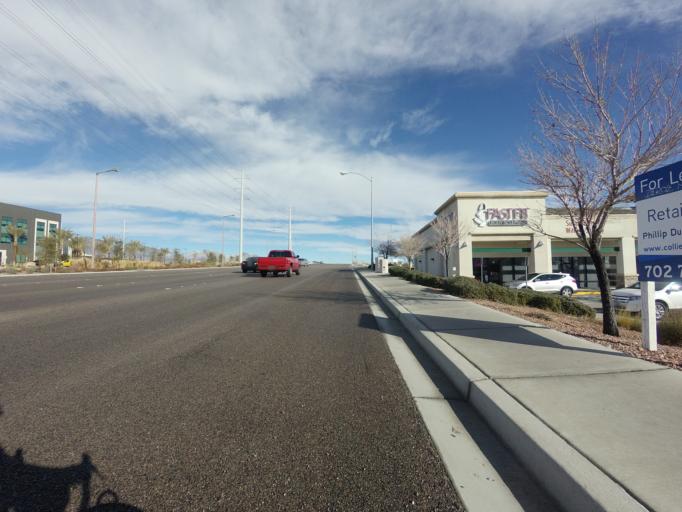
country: US
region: Nevada
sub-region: Clark County
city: Summerlin South
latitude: 36.1166
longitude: -115.3147
